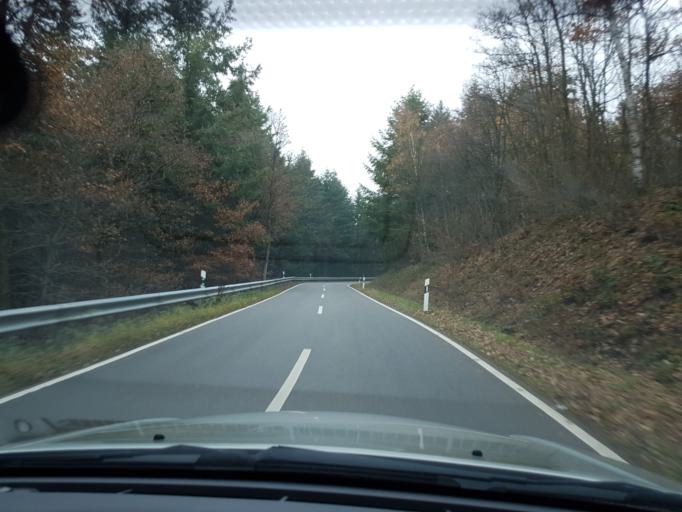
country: DE
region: Hesse
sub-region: Regierungsbezirk Darmstadt
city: Bad Schwalbach
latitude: 50.1111
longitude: 8.0321
